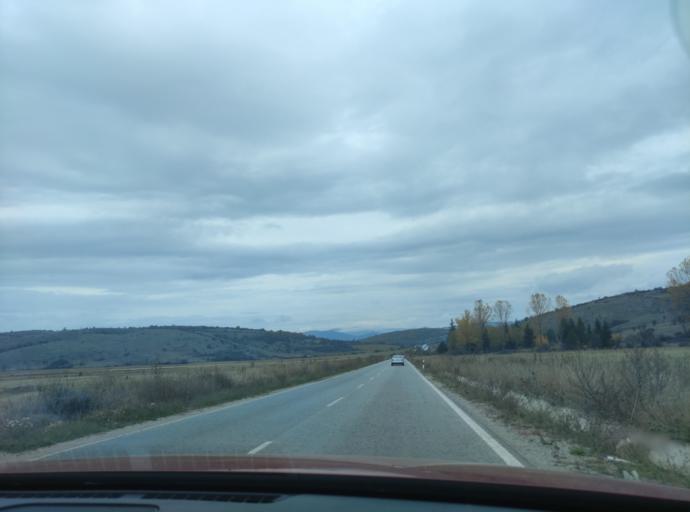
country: BG
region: Sofiya
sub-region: Obshtina Godech
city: Godech
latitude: 42.9493
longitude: 23.1591
